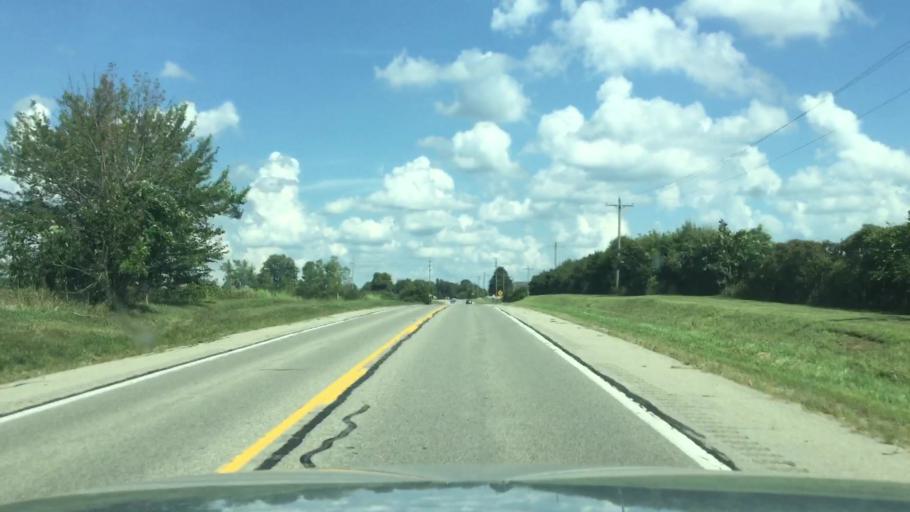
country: US
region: Michigan
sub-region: Lenawee County
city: Clinton
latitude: 42.0814
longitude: -83.9526
